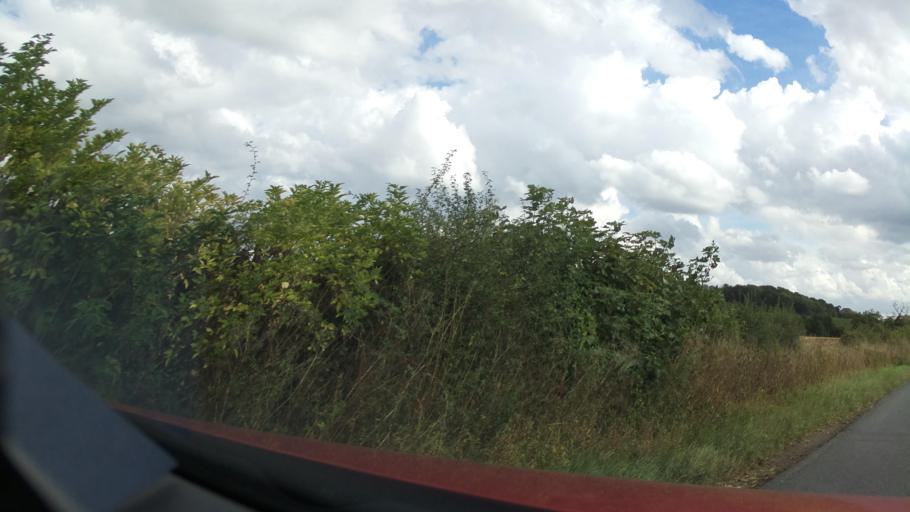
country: GB
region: England
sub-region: North Yorkshire
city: Bedale
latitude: 54.2190
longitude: -1.6324
